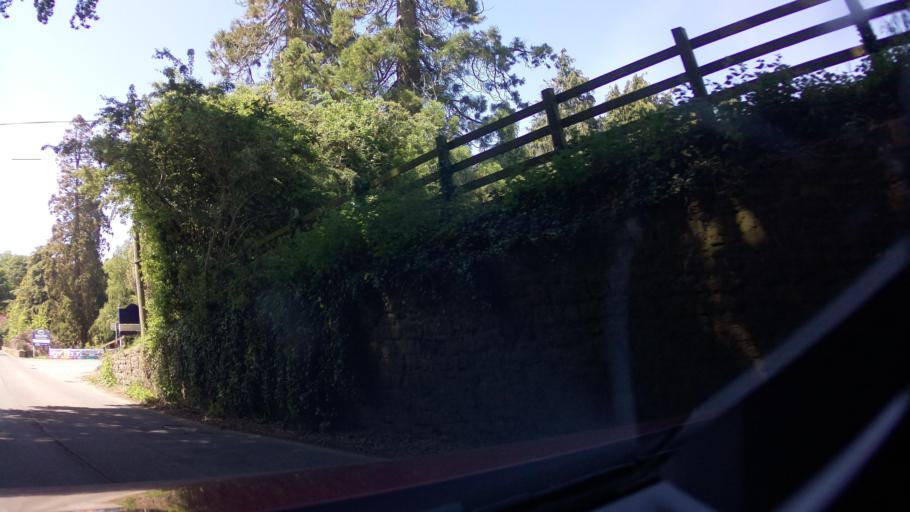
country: GB
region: England
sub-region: Devon
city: Budleigh Salterton
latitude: 50.6637
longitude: -3.3100
